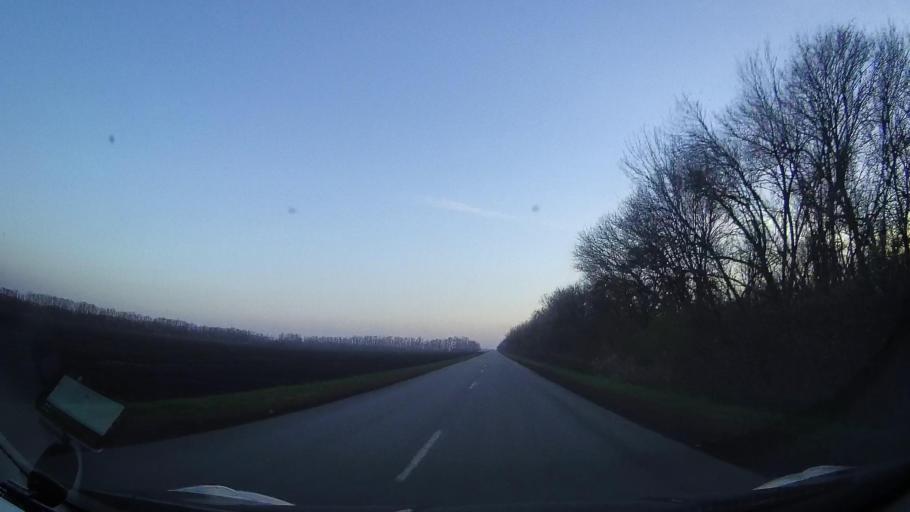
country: RU
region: Rostov
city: Zernograd
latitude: 46.9954
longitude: 40.3915
